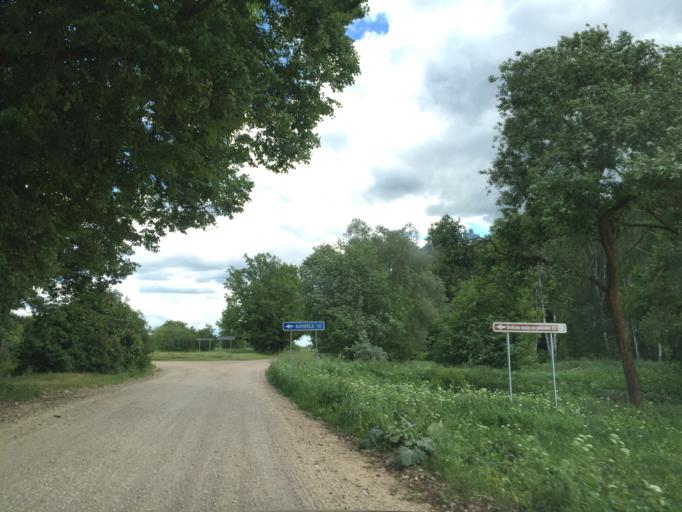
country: LV
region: Vecumnieki
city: Vecumnieki
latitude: 56.4665
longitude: 24.4277
